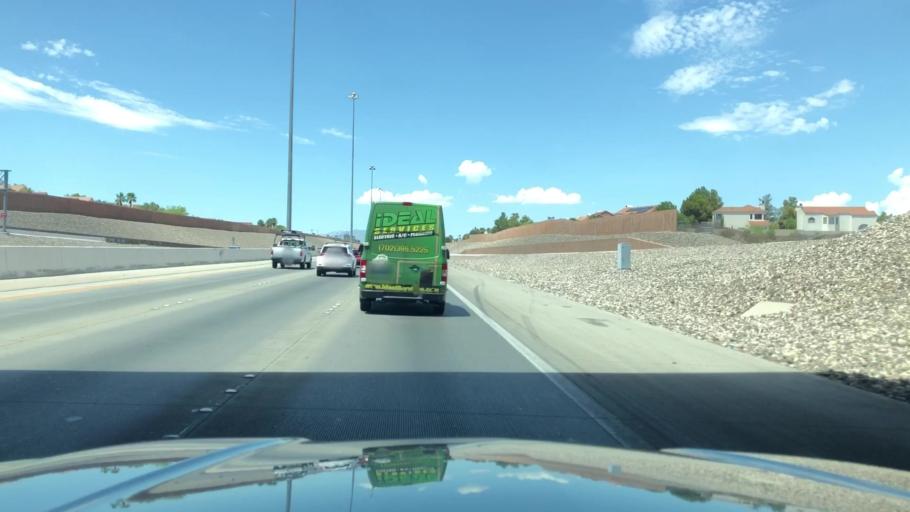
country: US
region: Nevada
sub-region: Clark County
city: Whitney
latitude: 36.0275
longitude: -115.0629
